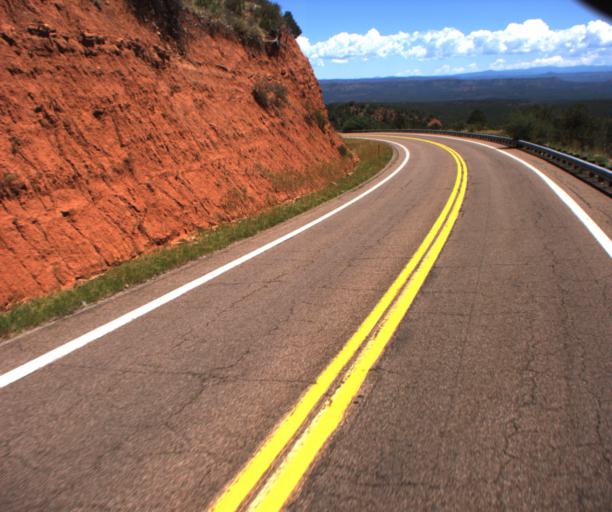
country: US
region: Arizona
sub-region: Navajo County
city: Cibecue
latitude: 33.9303
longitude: -110.3522
